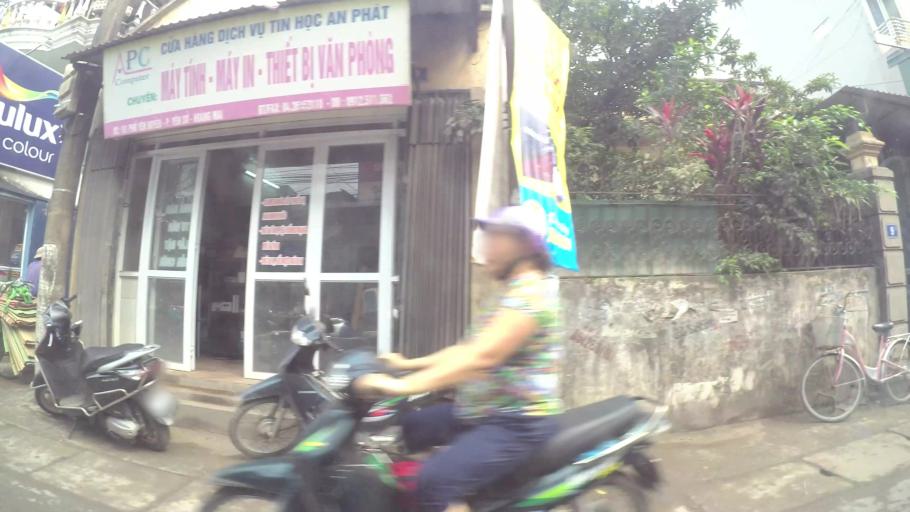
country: VN
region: Ha Noi
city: Van Dien
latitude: 20.9736
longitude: 105.8668
